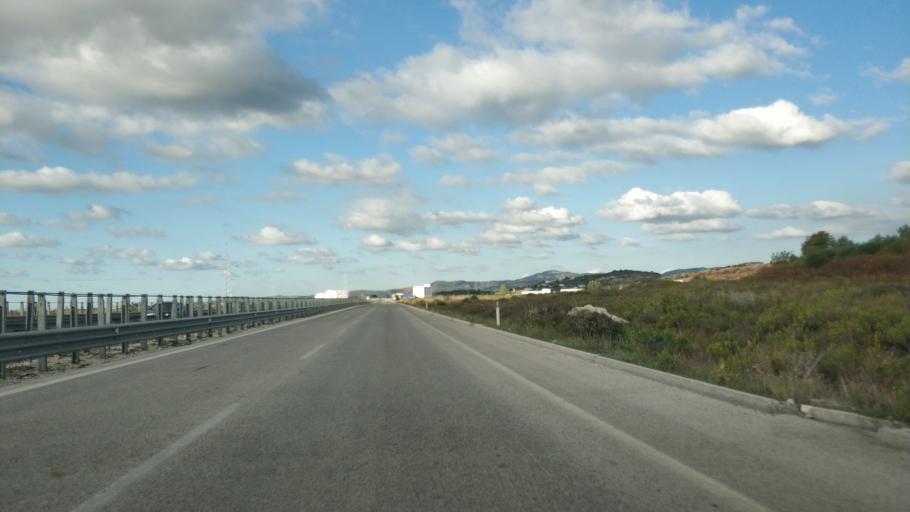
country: AL
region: Vlore
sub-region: Rrethi i Vlores
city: Novosele
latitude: 40.5899
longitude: 19.4742
